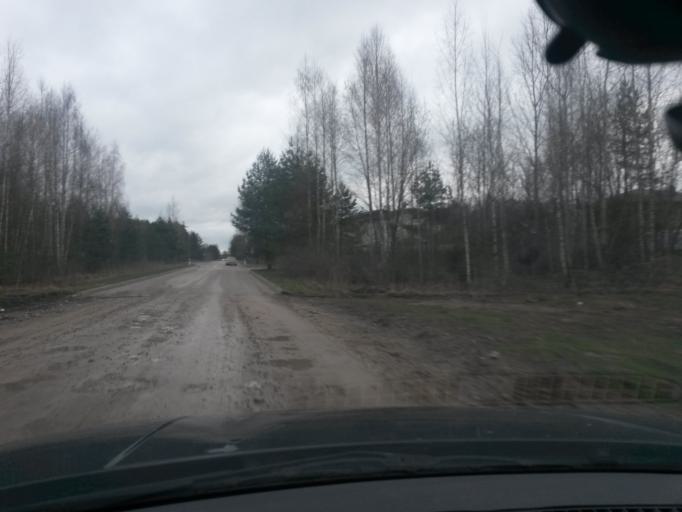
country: LV
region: Stopini
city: Ulbroka
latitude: 56.8969
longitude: 24.2475
